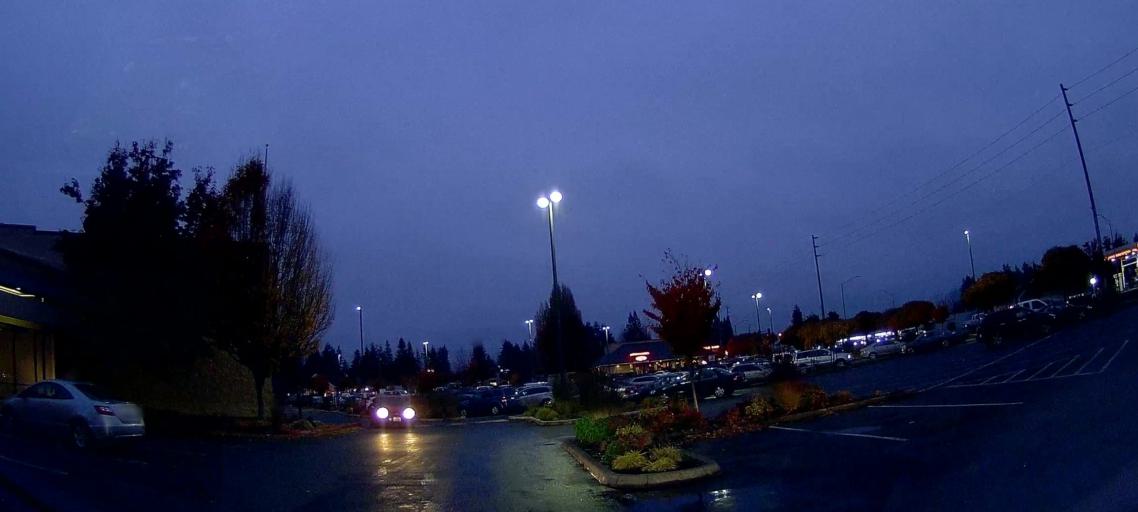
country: US
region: Washington
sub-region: Thurston County
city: Lacey
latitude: 47.0423
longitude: -122.8466
